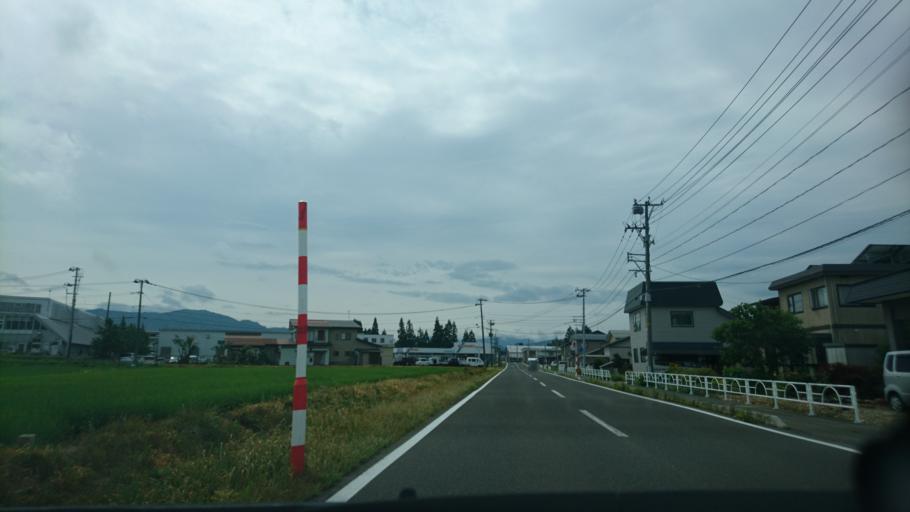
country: JP
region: Akita
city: Yuzawa
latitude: 39.1813
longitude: 140.5544
